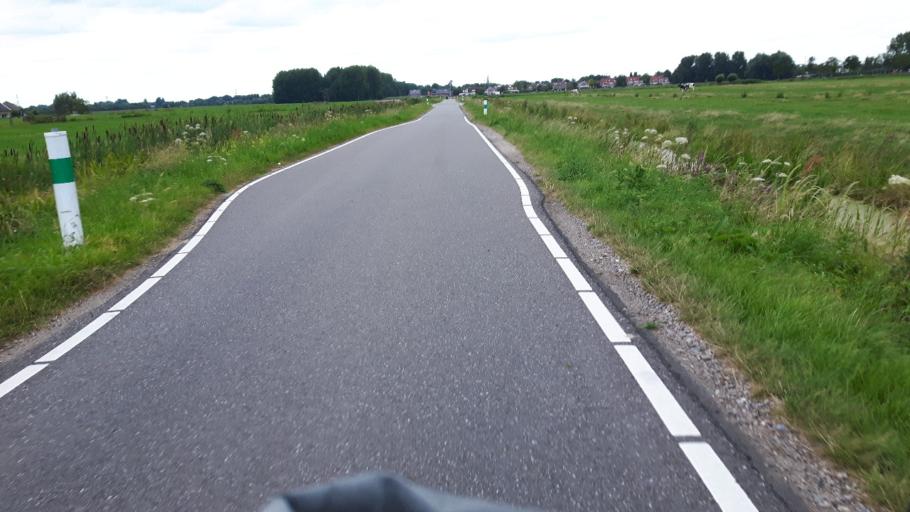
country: NL
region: South Holland
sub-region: Gemeente Vlist
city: Haastrecht
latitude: 51.9880
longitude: 4.7816
